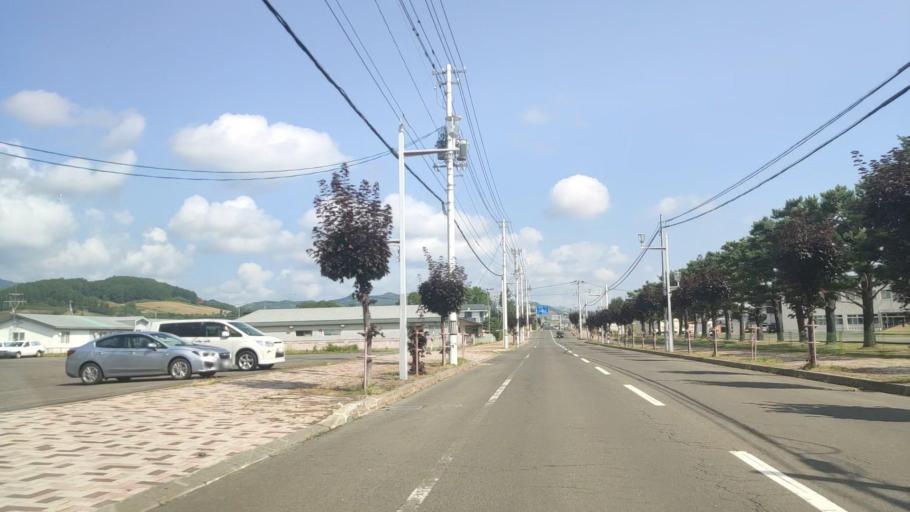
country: JP
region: Hokkaido
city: Shimo-furano
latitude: 43.3519
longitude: 142.3836
